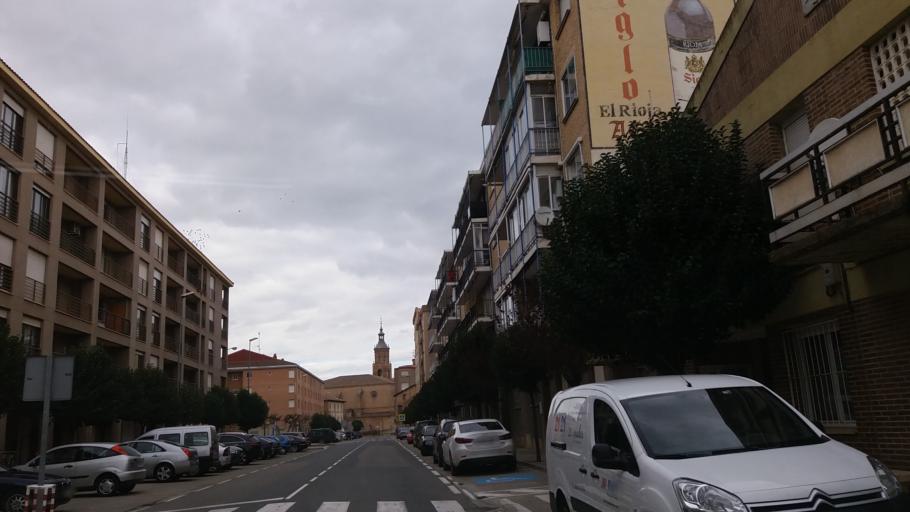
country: ES
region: La Rioja
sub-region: Provincia de La Rioja
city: Fuenmayor
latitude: 42.4648
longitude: -2.5602
